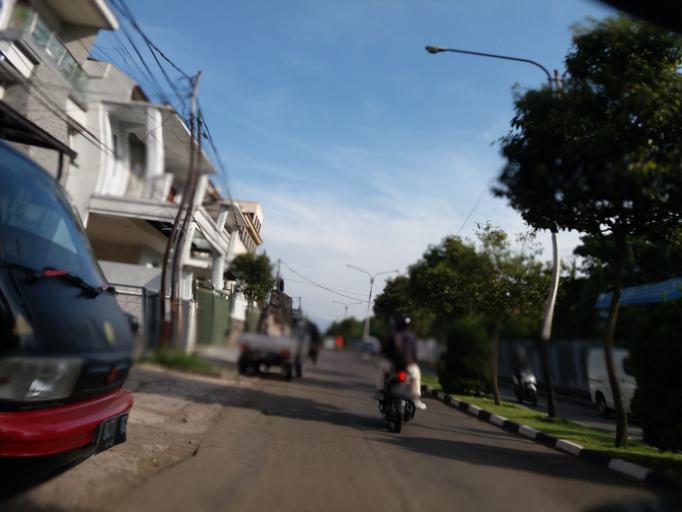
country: ID
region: West Java
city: Bandung
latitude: -6.9553
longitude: 107.6242
